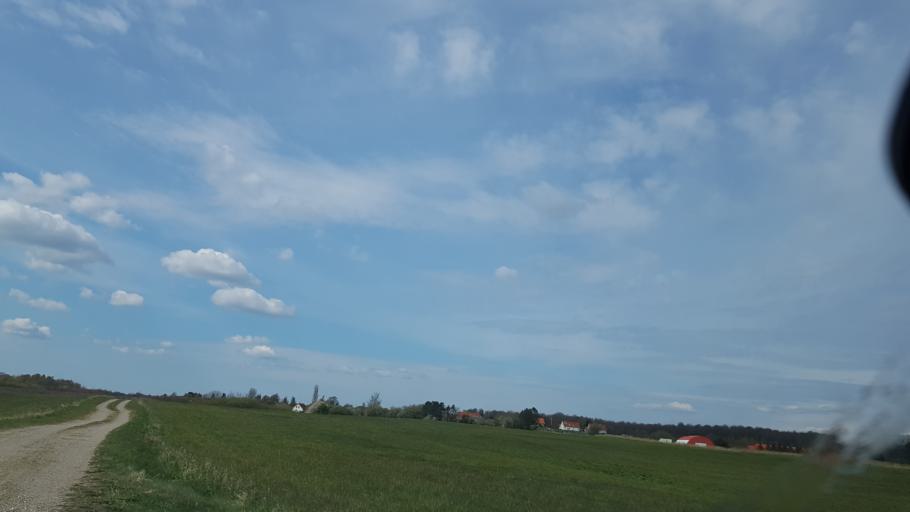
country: DK
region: Capital Region
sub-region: Allerod Kommune
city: Lillerod
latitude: 55.8944
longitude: 12.3385
